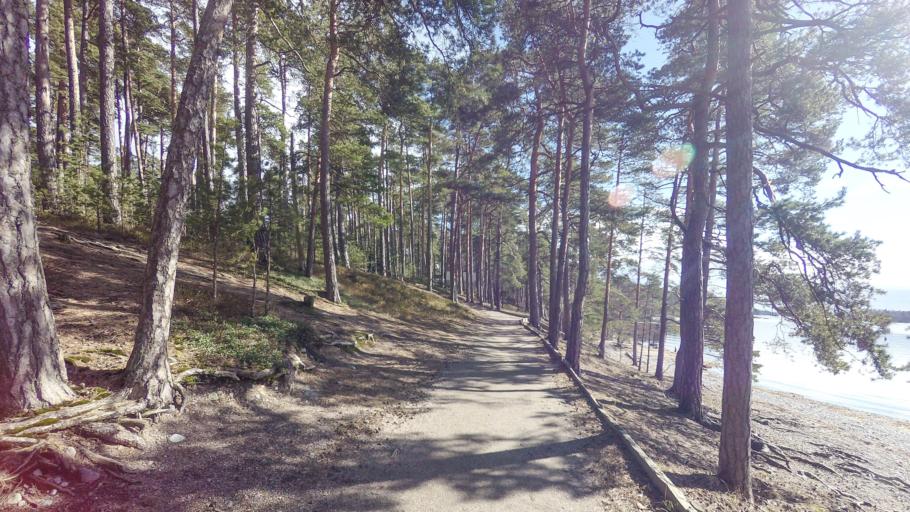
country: FI
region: Uusimaa
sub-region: Helsinki
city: Vantaa
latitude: 60.1965
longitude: 25.1327
